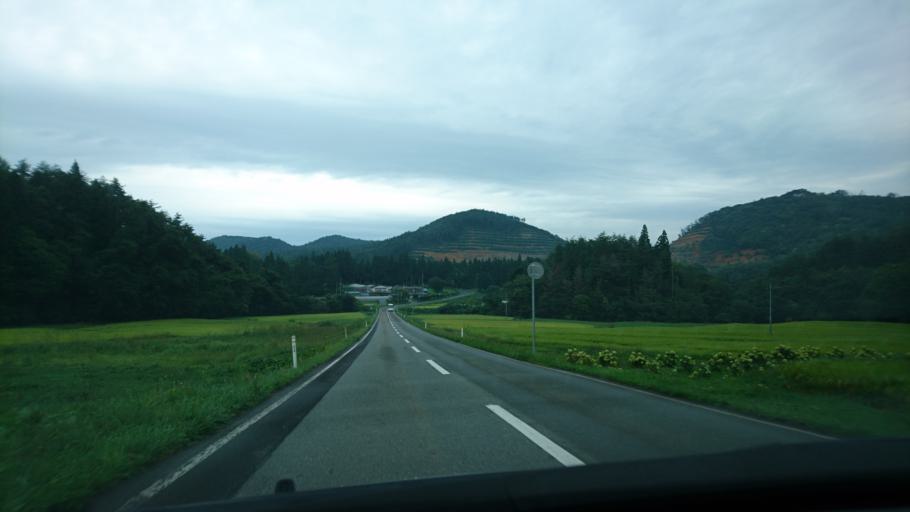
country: JP
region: Iwate
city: Ichinoseki
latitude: 39.0245
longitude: 141.2026
